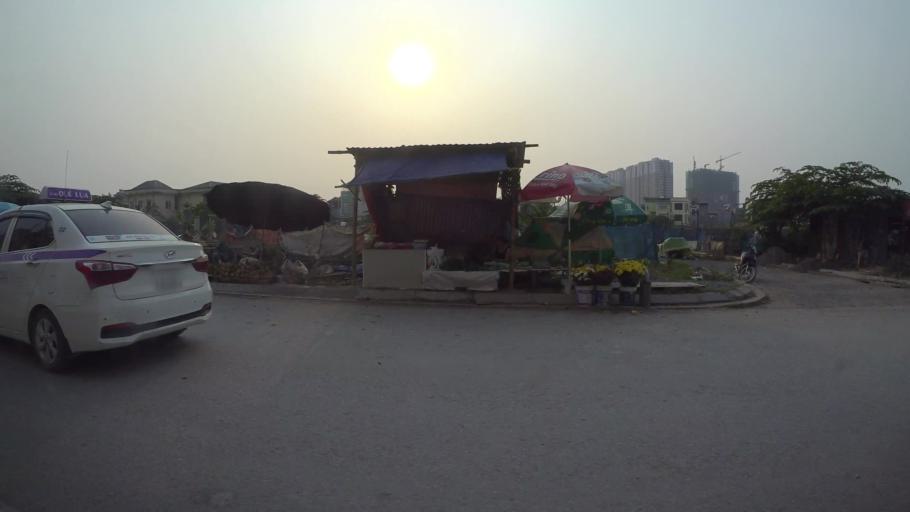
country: VN
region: Ha Noi
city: Cau Dien
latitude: 21.0062
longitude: 105.7265
